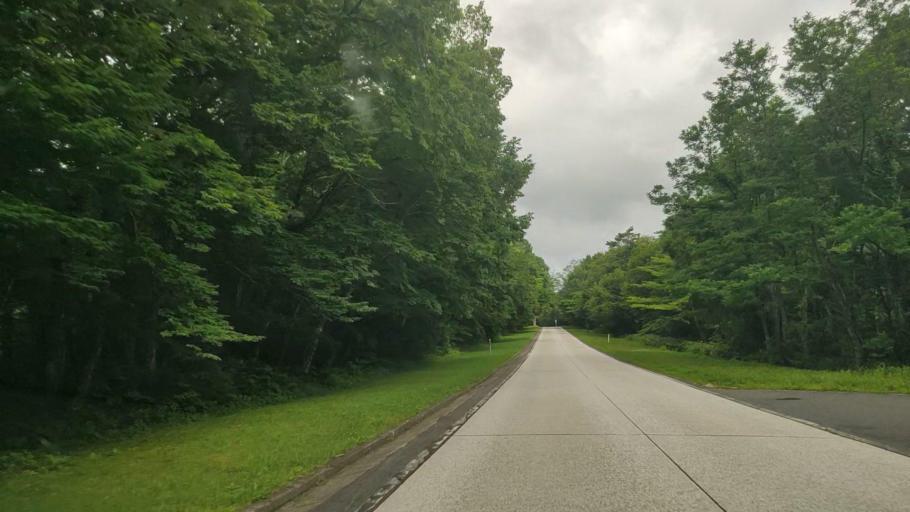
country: JP
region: Tottori
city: Yonago
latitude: 35.3966
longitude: 133.5157
